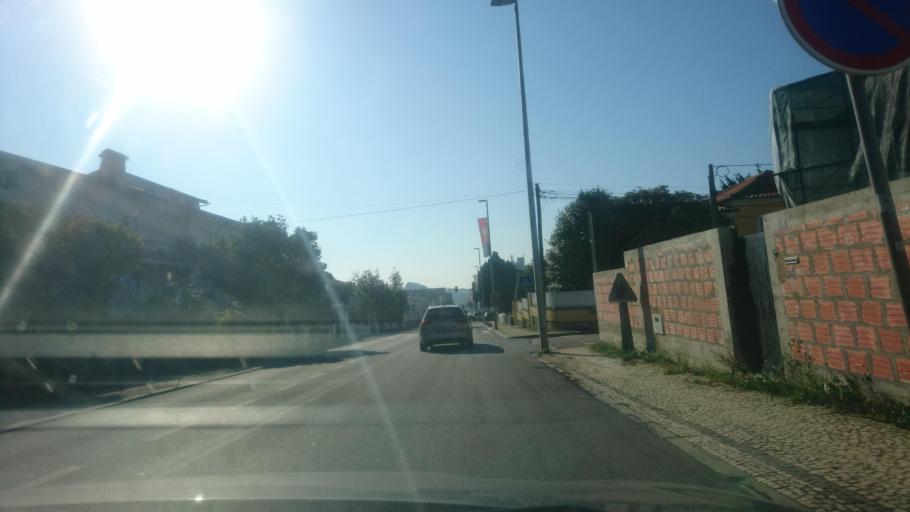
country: PT
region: Aveiro
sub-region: Santa Maria da Feira
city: Feira
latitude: 40.9283
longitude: -8.5481
